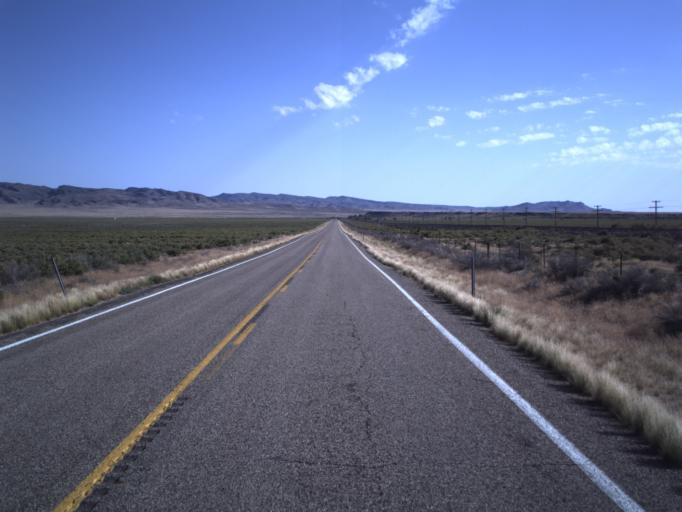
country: US
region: Utah
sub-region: Beaver County
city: Milford
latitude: 38.6861
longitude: -112.9765
